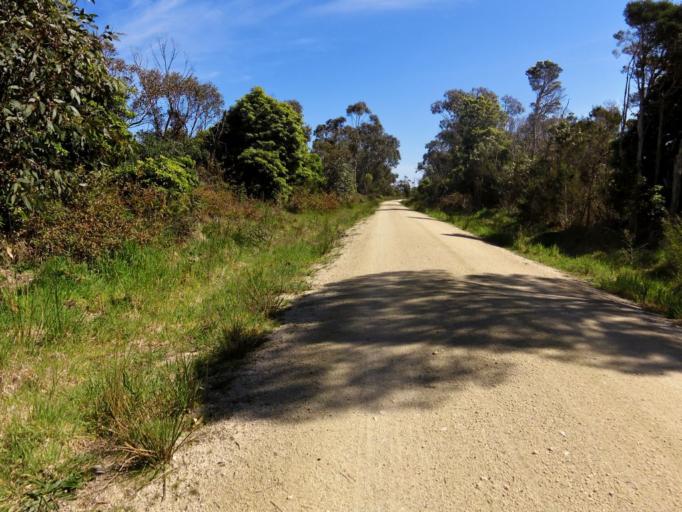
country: AU
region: Victoria
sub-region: Latrobe
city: Morwell
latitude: -38.6735
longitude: 146.3999
